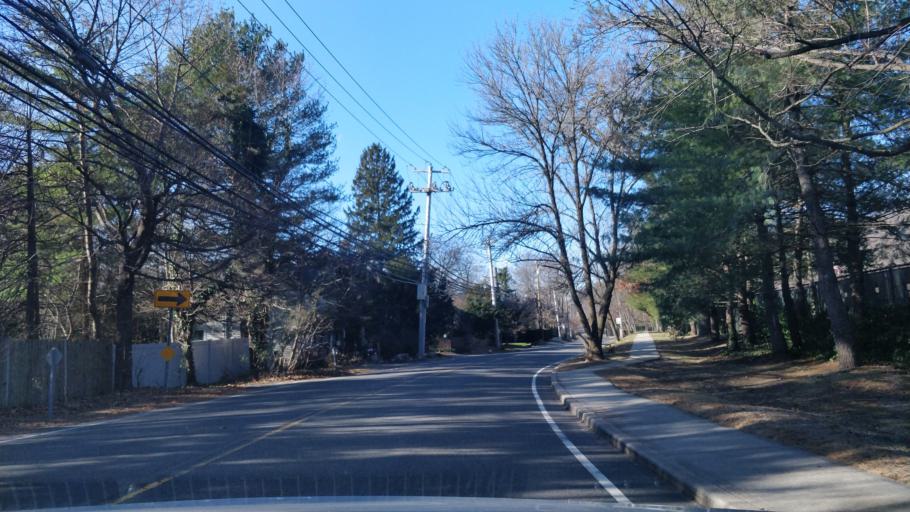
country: US
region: New York
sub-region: Nassau County
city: East Hills
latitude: 40.7945
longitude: -73.6261
